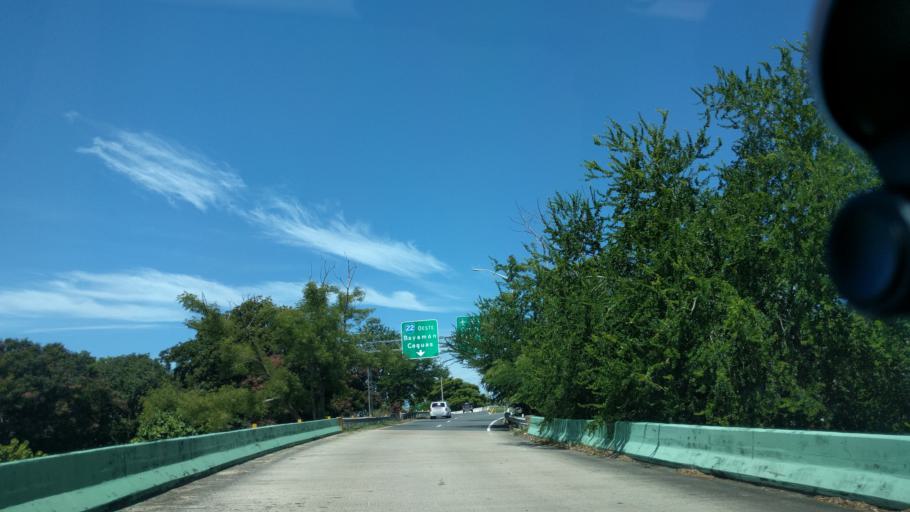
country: PR
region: San Juan
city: San Juan
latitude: 18.4406
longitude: -66.0690
